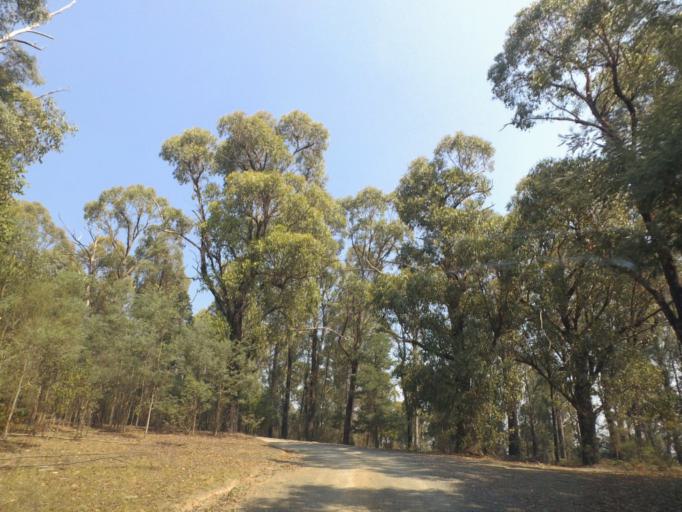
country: AU
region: Victoria
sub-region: Yarra Ranges
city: Millgrove
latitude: -37.5337
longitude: 145.7196
